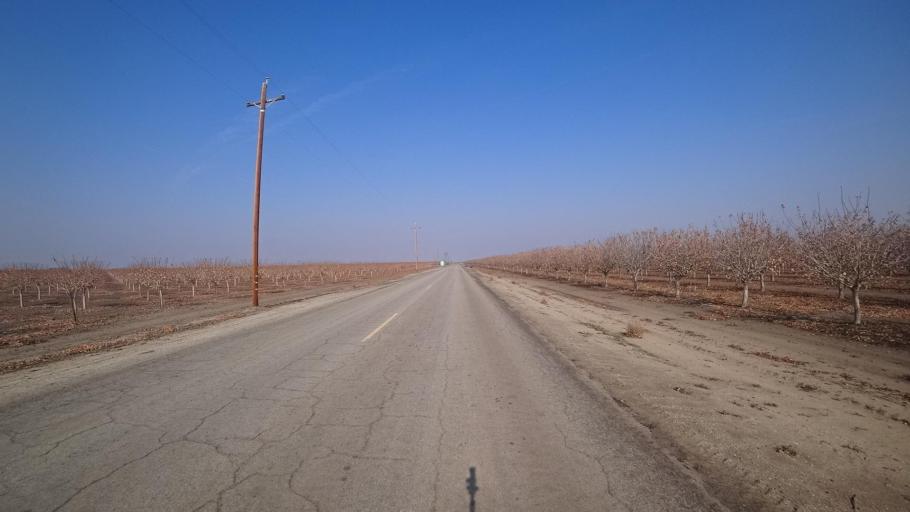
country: US
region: California
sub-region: Kern County
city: Buttonwillow
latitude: 35.3482
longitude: -119.3945
